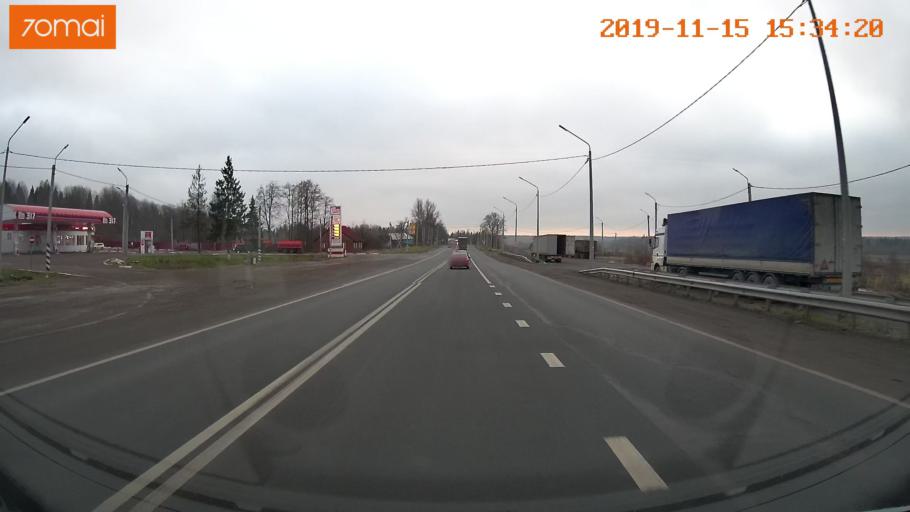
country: RU
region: Jaroslavl
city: Danilov
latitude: 58.0704
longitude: 40.0892
